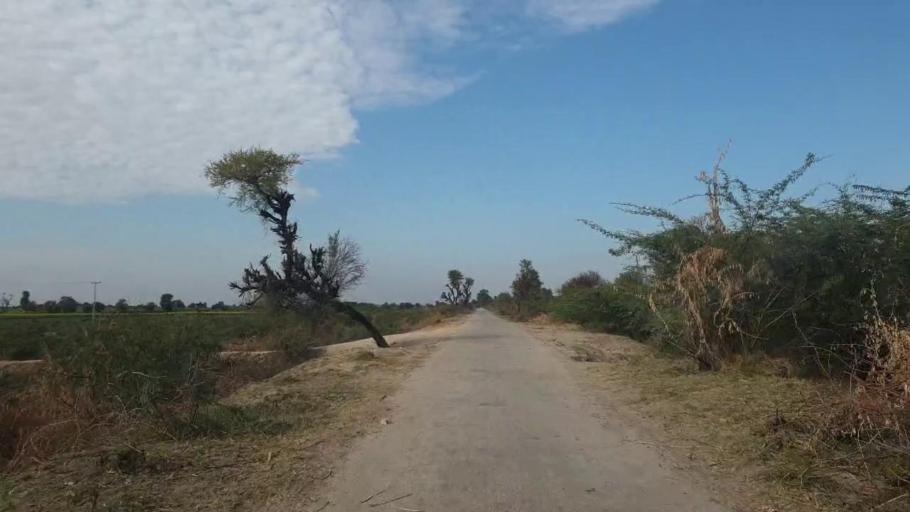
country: PK
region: Sindh
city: Sinjhoro
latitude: 26.0335
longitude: 68.8787
